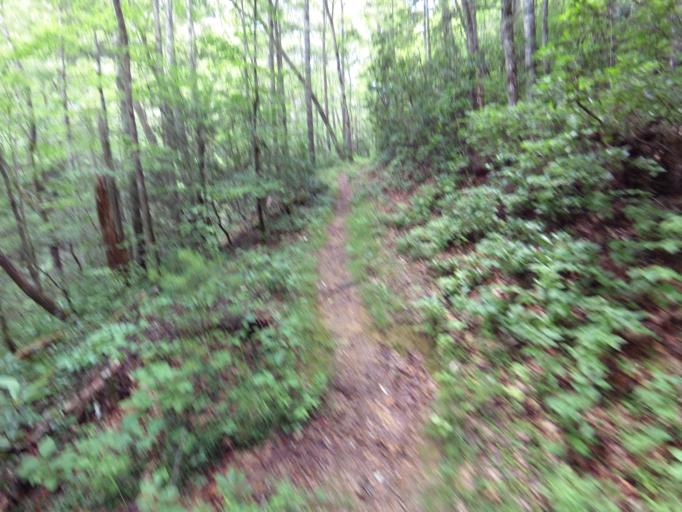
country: US
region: Tennessee
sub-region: Blount County
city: Wildwood
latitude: 35.6712
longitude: -83.8315
